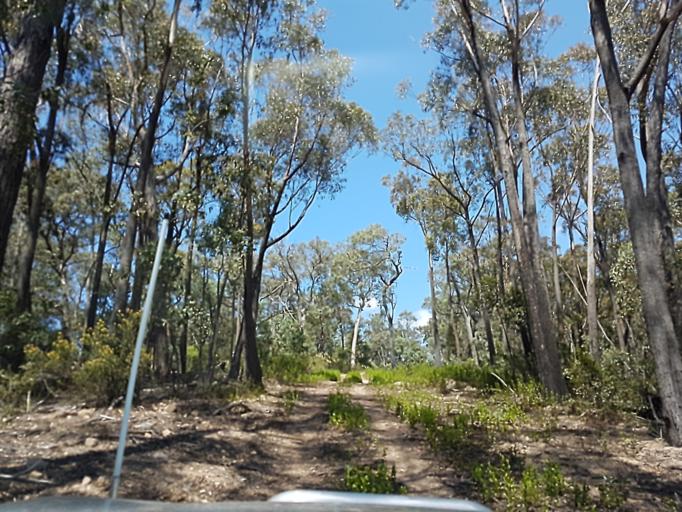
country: AU
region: Victoria
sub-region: East Gippsland
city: Lakes Entrance
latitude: -37.3090
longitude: 148.3597
